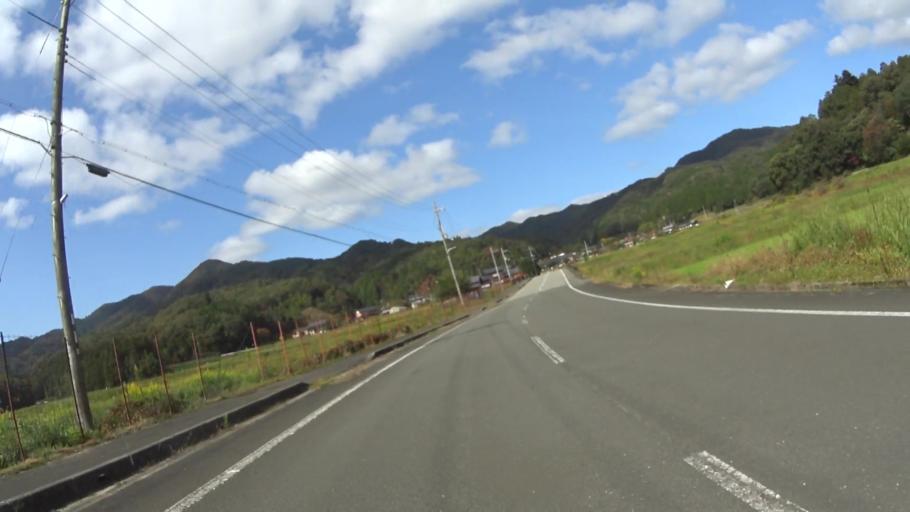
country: JP
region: Hyogo
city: Toyooka
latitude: 35.5045
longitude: 134.9922
